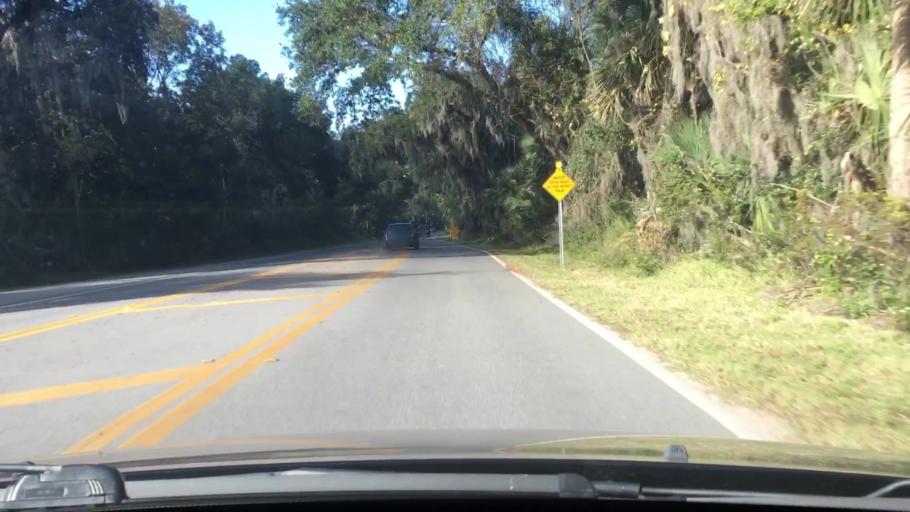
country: US
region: Florida
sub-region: Volusia County
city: Ormond-by-the-Sea
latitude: 29.3886
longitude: -81.1326
